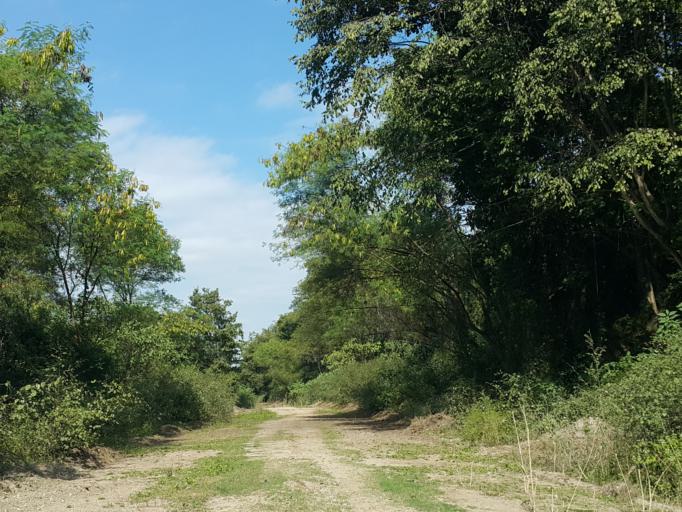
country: TH
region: Lampang
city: Mae Mo
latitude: 18.3347
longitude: 99.7678
